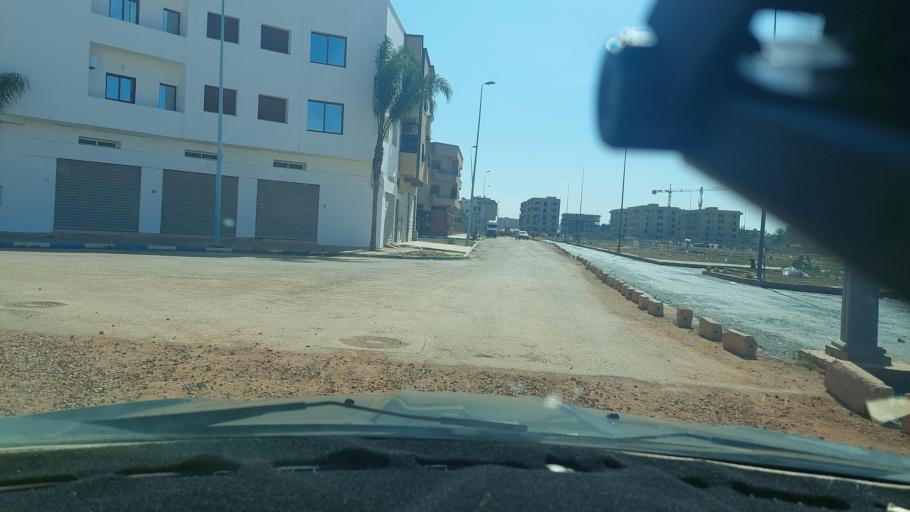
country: MA
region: Grand Casablanca
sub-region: Mediouna
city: Mediouna
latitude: 33.3789
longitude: -7.5380
